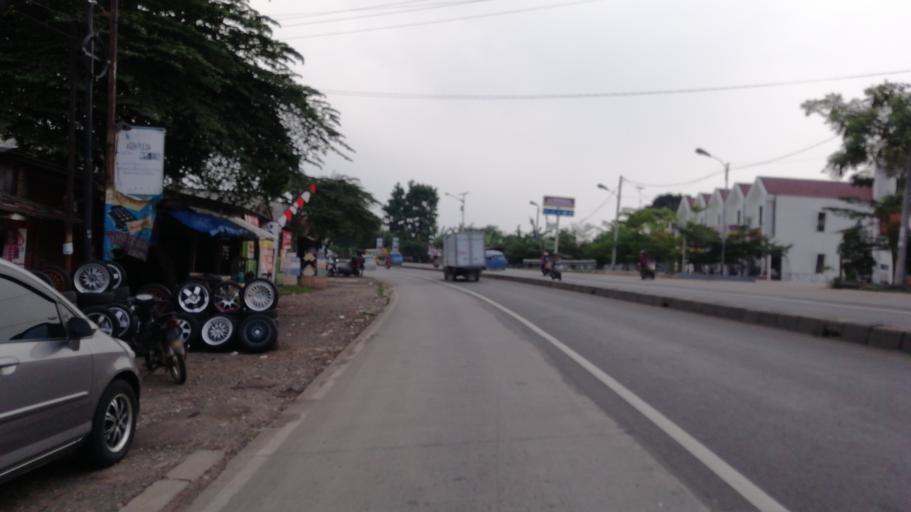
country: ID
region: West Java
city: Parung
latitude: -6.4884
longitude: 106.7361
